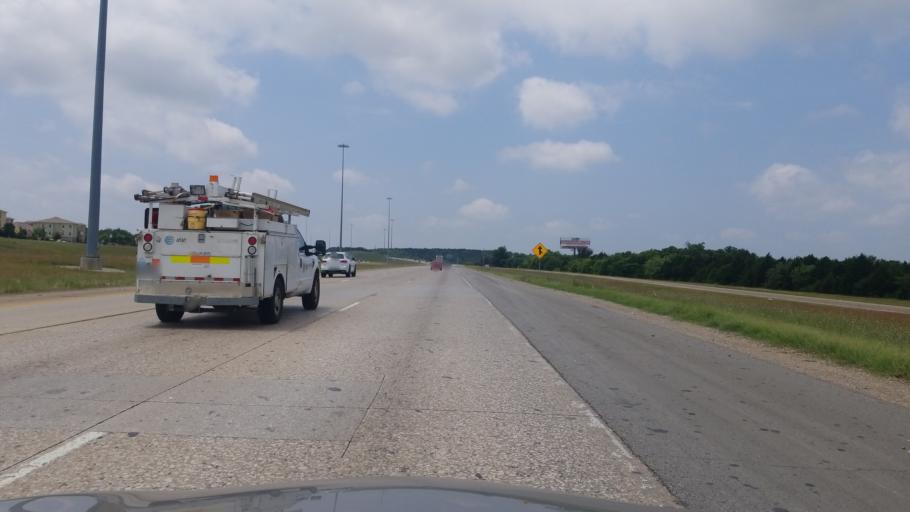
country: US
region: Texas
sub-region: Dallas County
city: Duncanville
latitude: 32.6904
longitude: -96.9396
